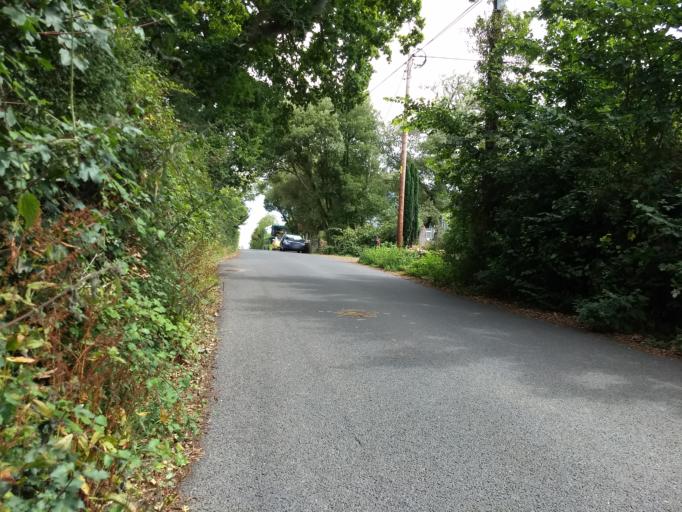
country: GB
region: England
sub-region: Isle of Wight
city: Ryde
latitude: 50.7097
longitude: -1.1793
